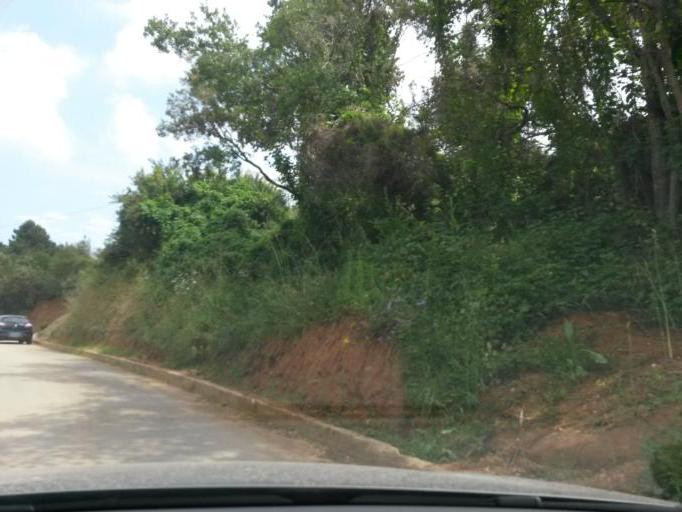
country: IT
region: Tuscany
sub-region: Provincia di Livorno
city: Porto Azzurro
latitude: 42.7462
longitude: 10.4032
